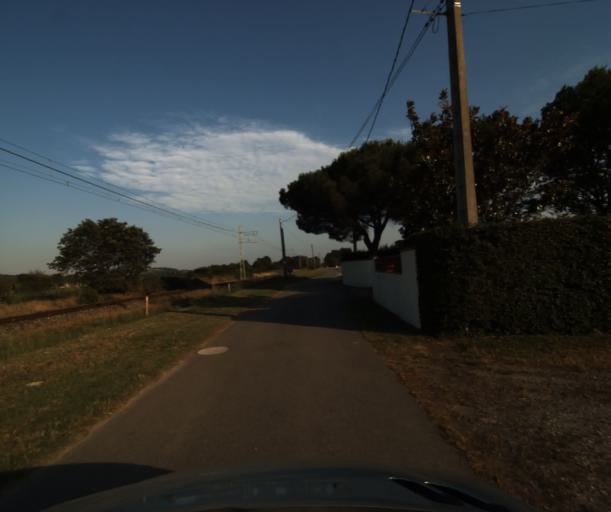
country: FR
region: Midi-Pyrenees
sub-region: Departement de la Haute-Garonne
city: Lacroix-Falgarde
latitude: 43.4868
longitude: 1.3956
